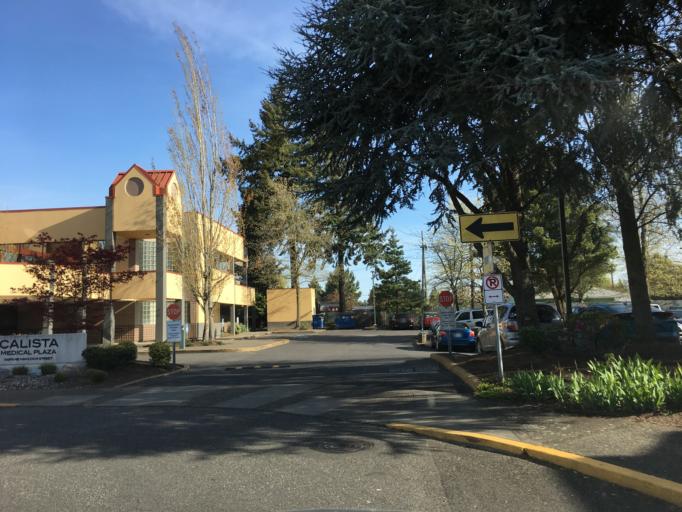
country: US
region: Oregon
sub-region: Multnomah County
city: Lents
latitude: 45.5362
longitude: -122.5554
